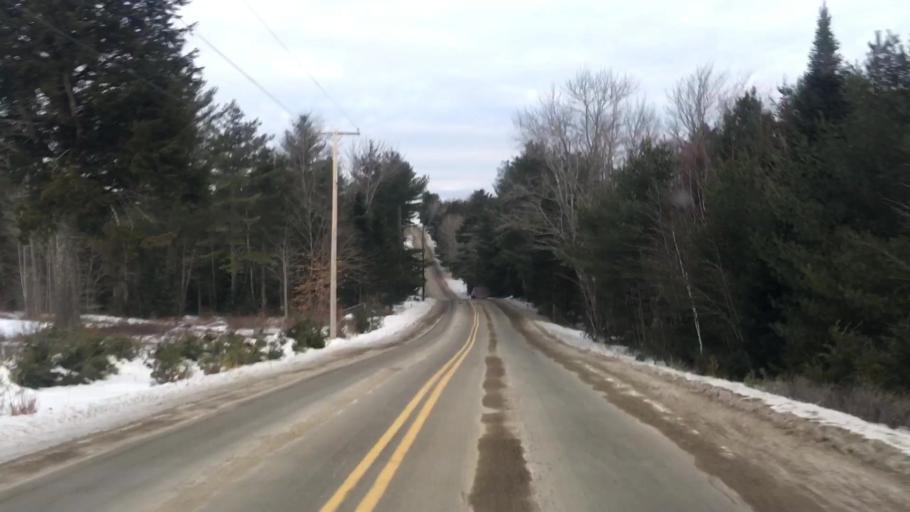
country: US
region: Maine
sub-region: Hancock County
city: Franklin
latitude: 44.8399
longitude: -68.3236
